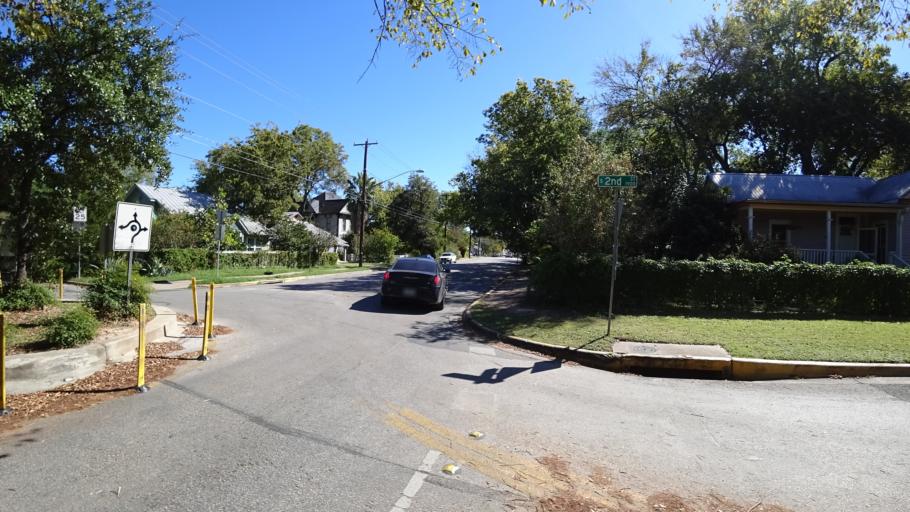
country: US
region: Texas
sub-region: Travis County
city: Austin
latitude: 30.2469
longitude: -97.7578
